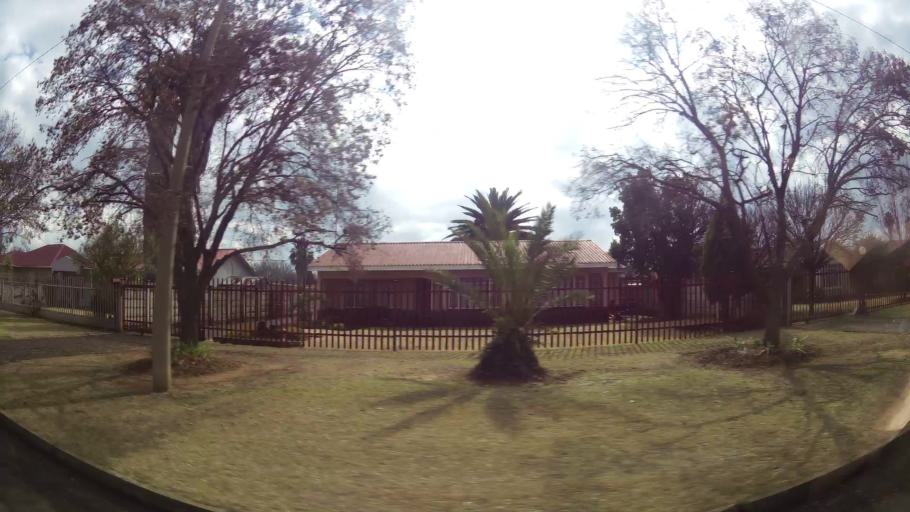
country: ZA
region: Gauteng
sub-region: Sedibeng District Municipality
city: Vereeniging
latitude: -26.6537
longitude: 27.9892
